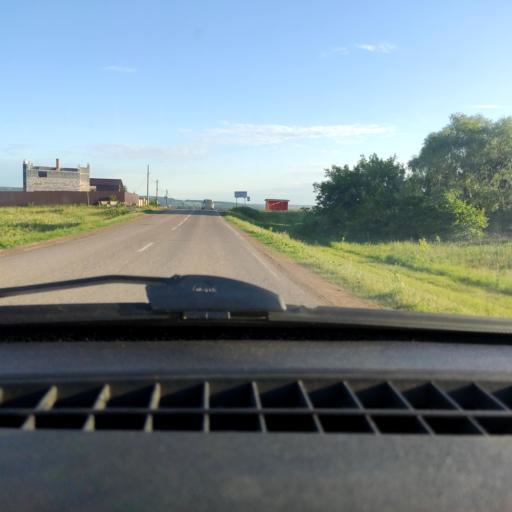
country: RU
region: Bashkortostan
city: Avdon
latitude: 54.6337
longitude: 55.6969
